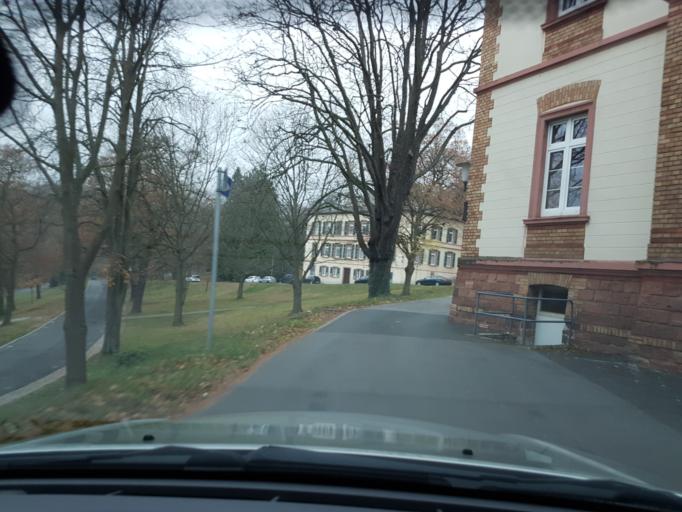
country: DE
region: Hesse
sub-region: Regierungsbezirk Darmstadt
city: Kiedrich
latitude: 50.0382
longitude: 8.0586
